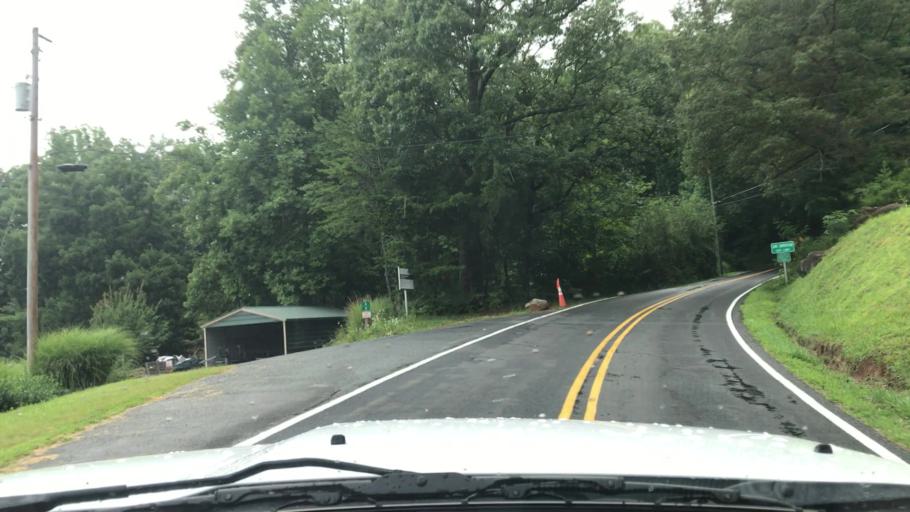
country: US
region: North Carolina
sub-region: Graham County
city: Robbinsville
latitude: 35.3661
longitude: -83.8578
